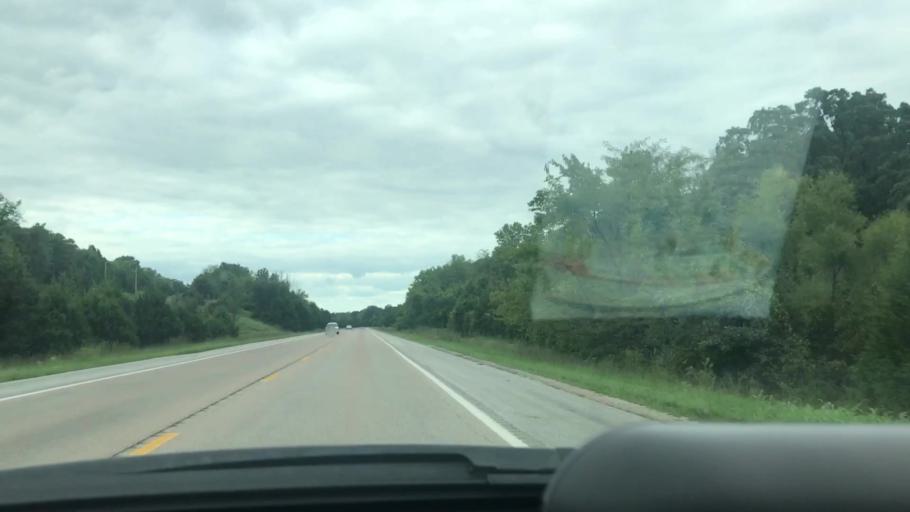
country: US
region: Missouri
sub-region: Benton County
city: Warsaw
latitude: 38.1977
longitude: -93.3252
